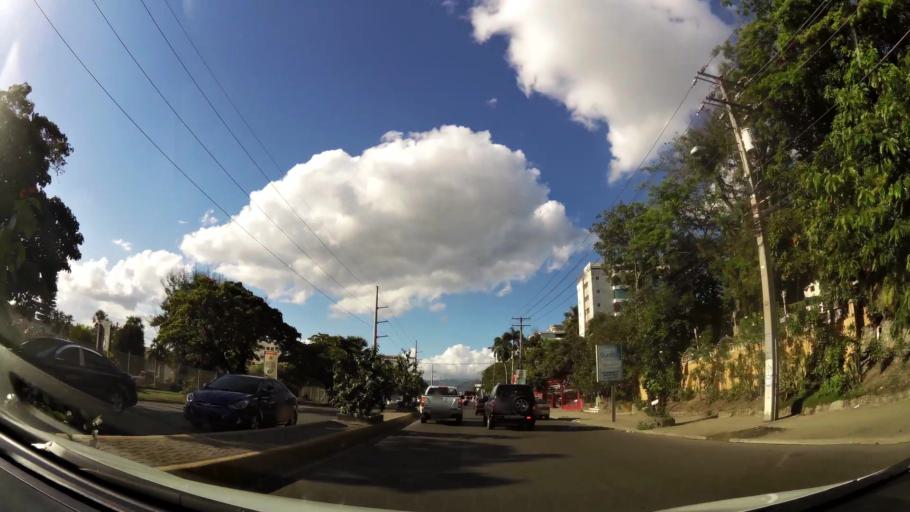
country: DO
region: Santiago
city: Santiago de los Caballeros
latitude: 19.4637
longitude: -70.6865
